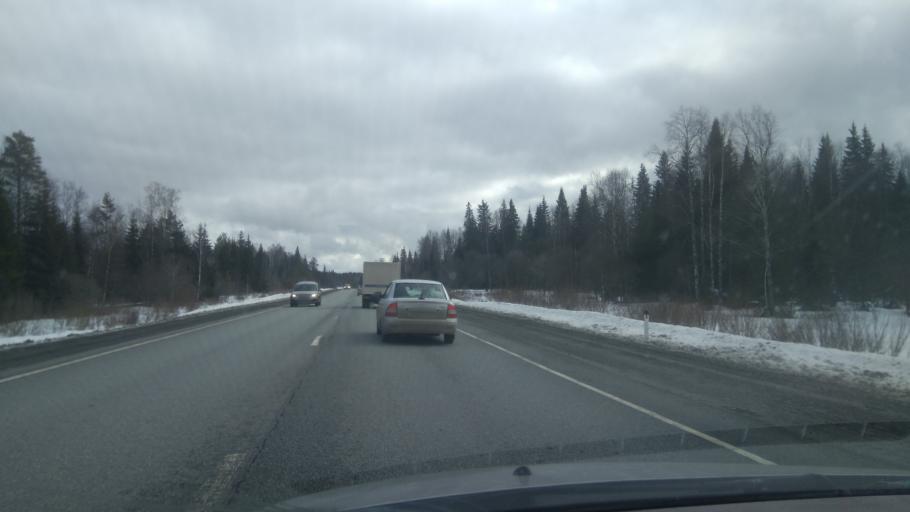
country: RU
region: Sverdlovsk
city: Atig
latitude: 56.8115
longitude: 59.3621
